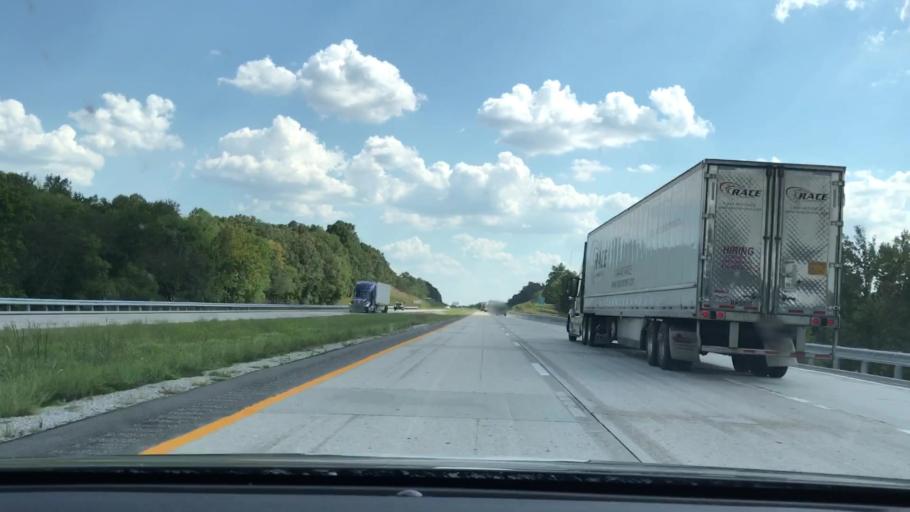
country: US
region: Kentucky
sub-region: Ohio County
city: Oak Grove
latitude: 37.3788
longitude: -86.8058
